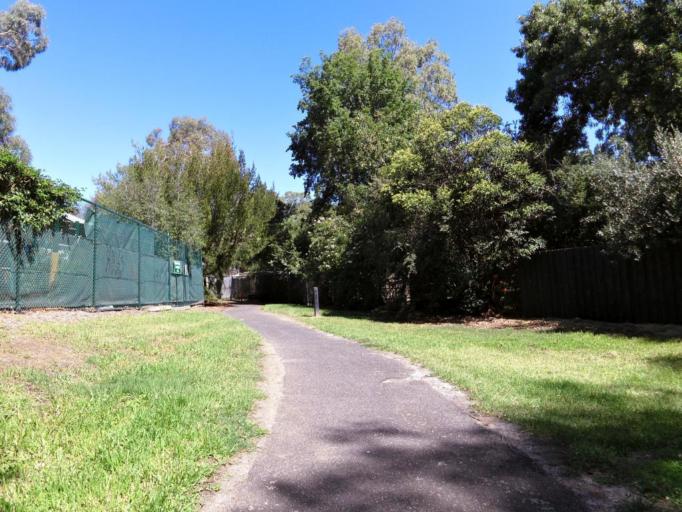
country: AU
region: Victoria
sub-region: Boroondara
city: Kew East
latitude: -37.8004
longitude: 145.0456
